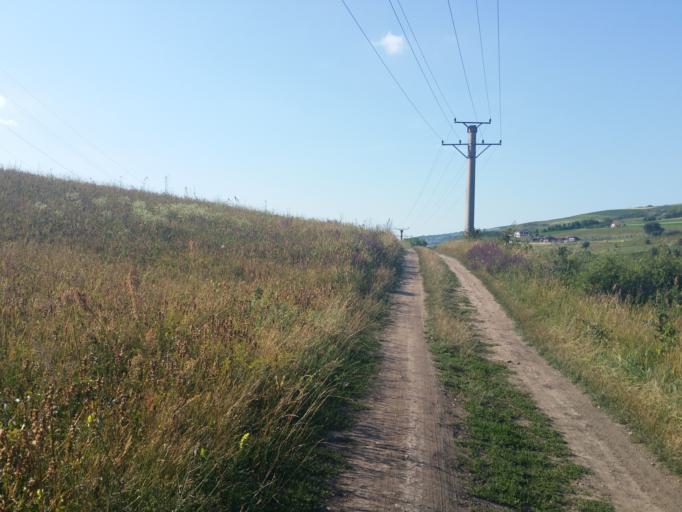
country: RO
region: Cluj
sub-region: Comuna Baciu
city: Baciu
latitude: 46.8035
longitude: 23.5298
